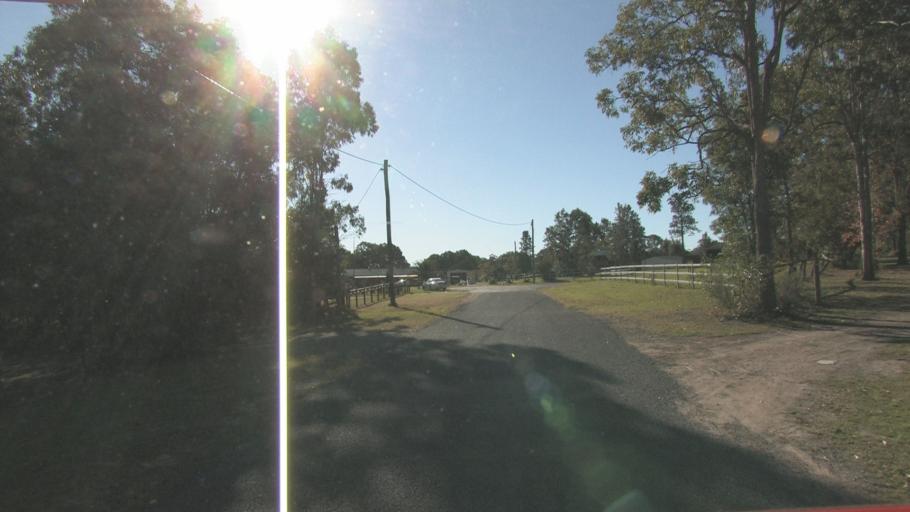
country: AU
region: Queensland
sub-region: Logan
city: Logan Reserve
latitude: -27.7442
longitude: 153.1056
